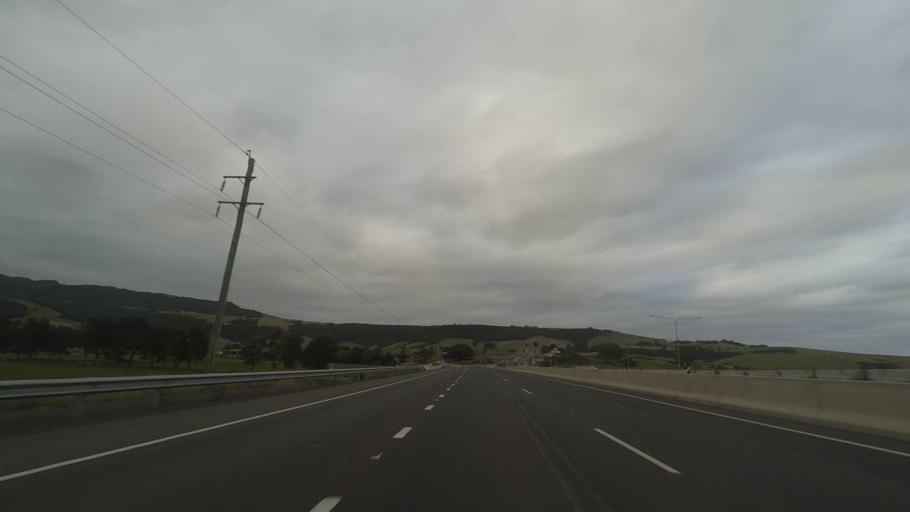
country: AU
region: New South Wales
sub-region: Kiama
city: Gerringong
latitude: -34.7255
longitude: 150.8288
